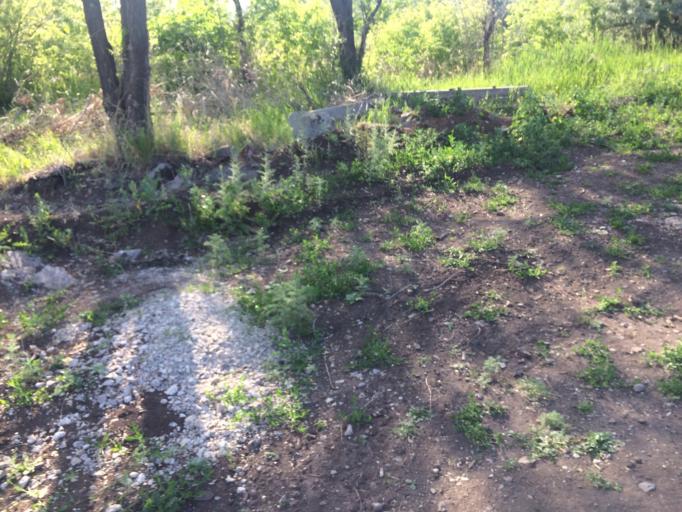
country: RU
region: Chelyabinsk
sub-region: Gorod Magnitogorsk
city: Magnitogorsk
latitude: 53.4007
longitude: 58.9947
